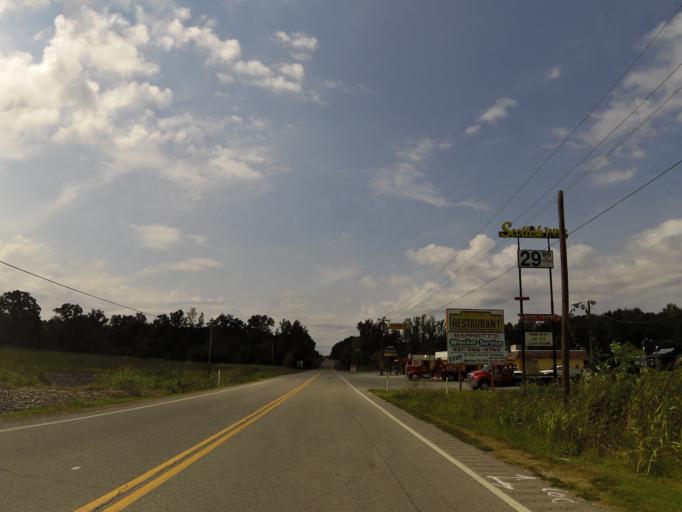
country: US
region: Tennessee
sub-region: Humphreys County
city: Waverly
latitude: 35.8780
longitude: -87.8028
